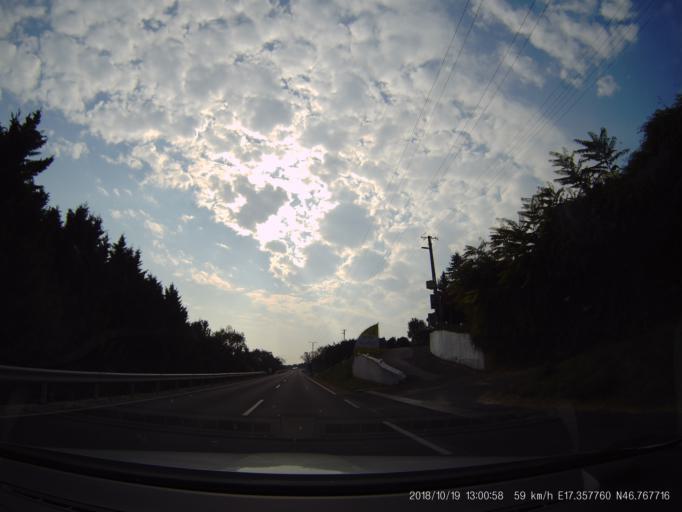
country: HU
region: Zala
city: Vonyarcvashegy
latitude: 46.7677
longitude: 17.3579
